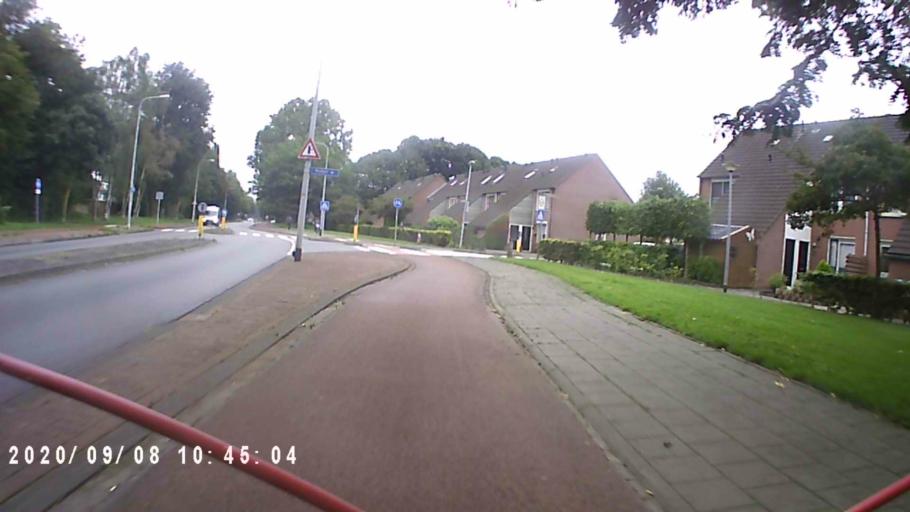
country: NL
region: Groningen
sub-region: Gemeente Groningen
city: Oosterpark
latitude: 53.2335
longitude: 6.6172
